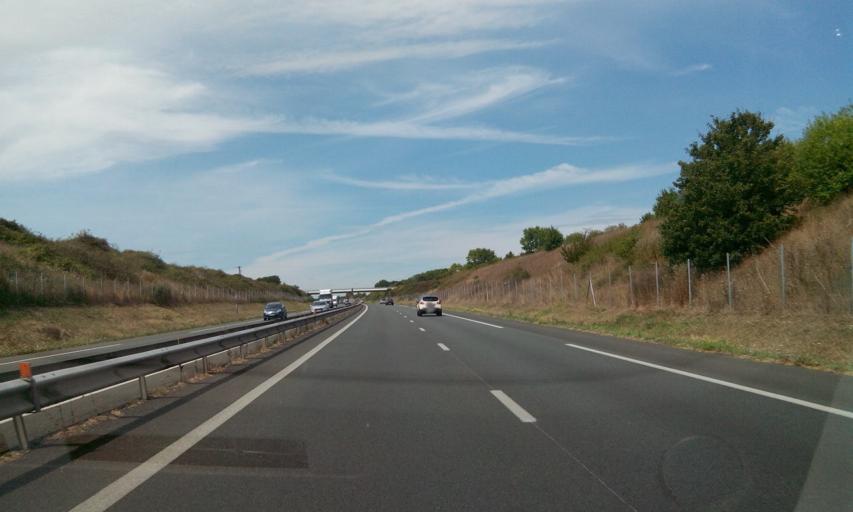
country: FR
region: Pays de la Loire
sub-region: Departement de la Vendee
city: Sainte-Hermine
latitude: 46.5488
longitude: -1.0892
